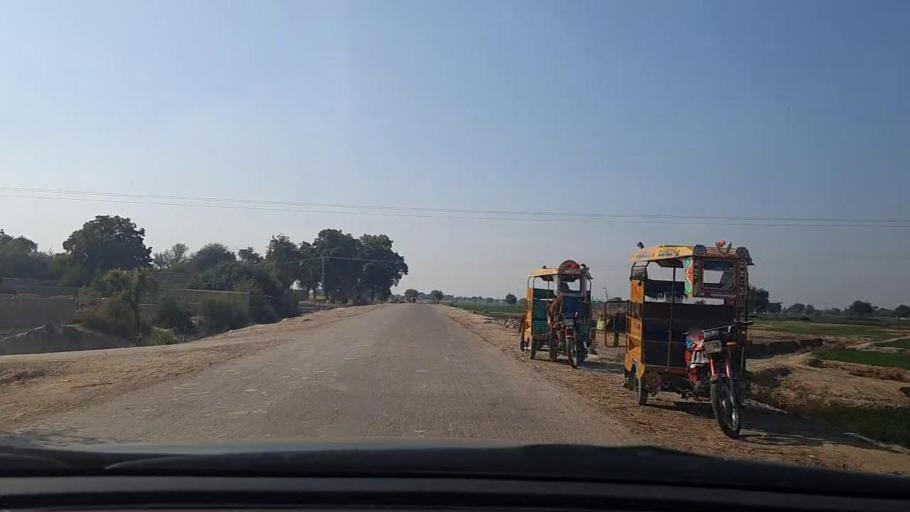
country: PK
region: Sindh
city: Daulatpur
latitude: 26.3178
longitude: 68.0568
